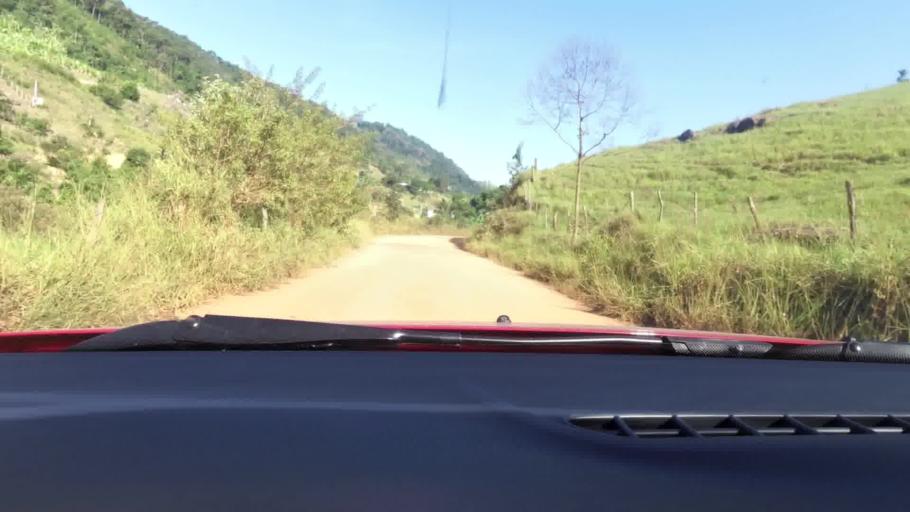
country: BR
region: Espirito Santo
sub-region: Guarapari
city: Guarapari
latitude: -20.5350
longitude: -40.5618
